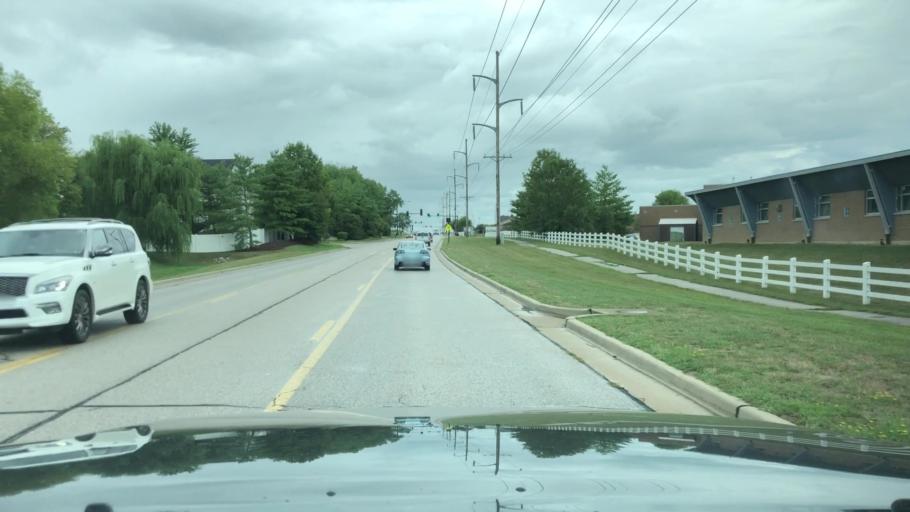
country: US
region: Missouri
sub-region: Saint Charles County
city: Dardenne Prairie
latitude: 38.7659
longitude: -90.7501
